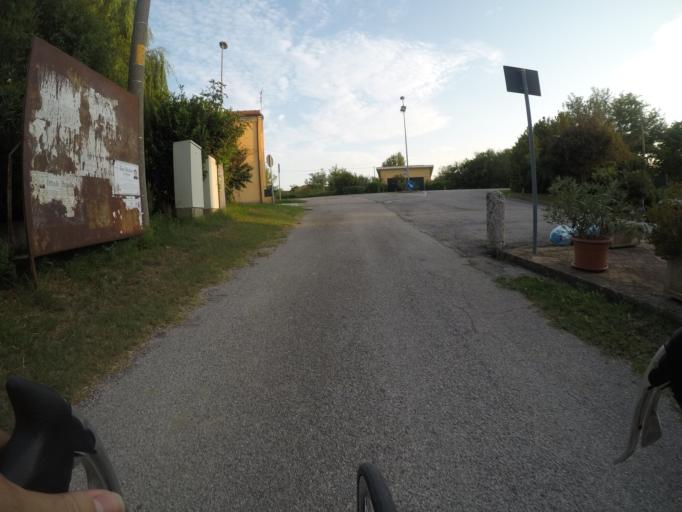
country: IT
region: Veneto
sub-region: Provincia di Rovigo
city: Pincara
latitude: 45.0017
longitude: 11.6193
